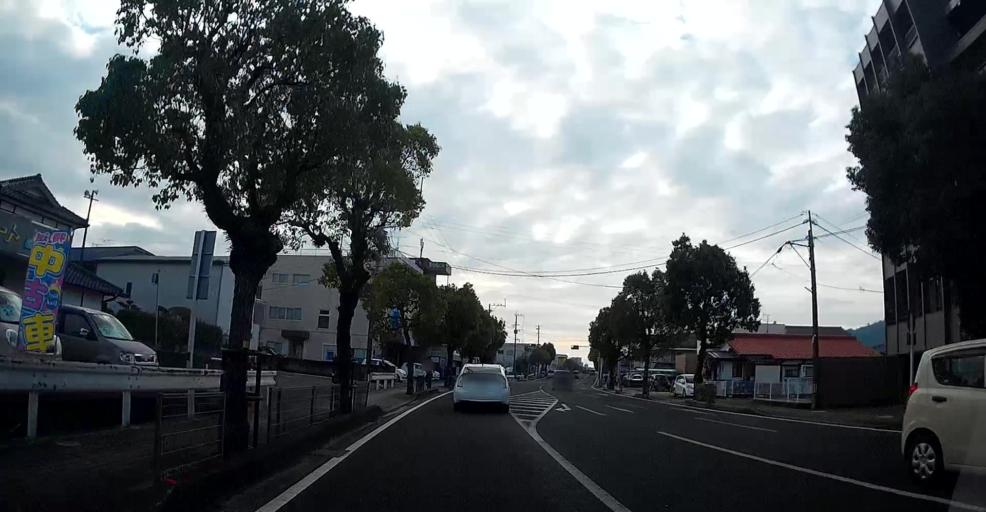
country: JP
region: Kumamoto
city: Hondo
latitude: 32.4643
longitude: 130.1901
